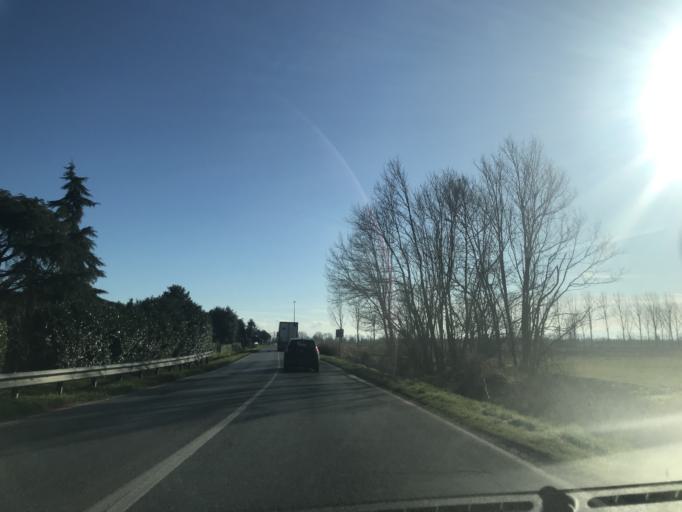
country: IT
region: Lombardy
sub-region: Provincia di Lodi
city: San Martino in Strada
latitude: 45.2758
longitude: 9.5234
